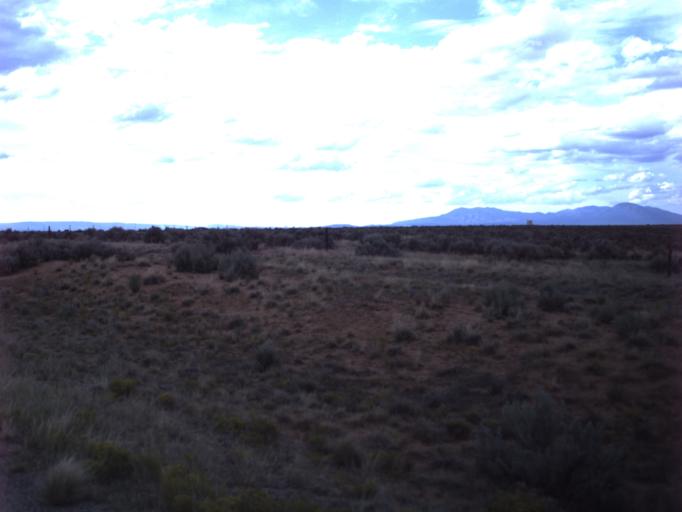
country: US
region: Utah
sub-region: San Juan County
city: Blanding
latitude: 37.4294
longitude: -109.3594
